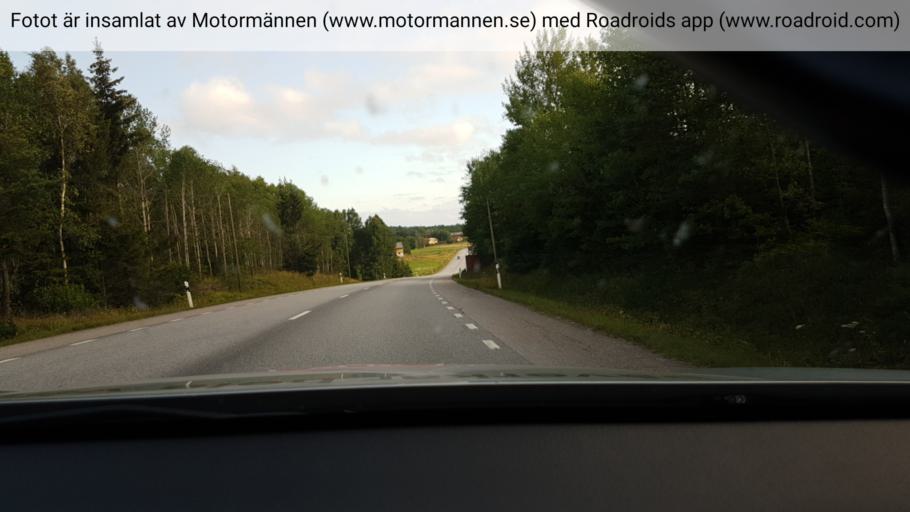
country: SE
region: Stockholm
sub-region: Norrtalje Kommun
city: Rimbo
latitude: 59.6416
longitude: 18.3319
